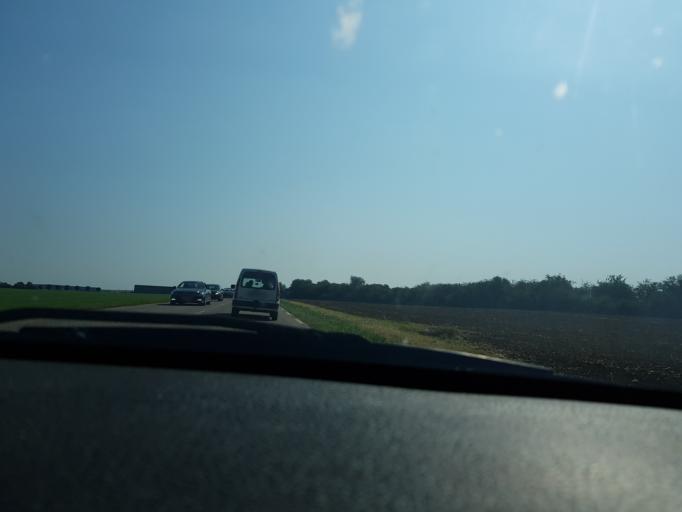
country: FR
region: Lorraine
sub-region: Departement de la Moselle
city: Verny
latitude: 48.9634
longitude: 6.2136
